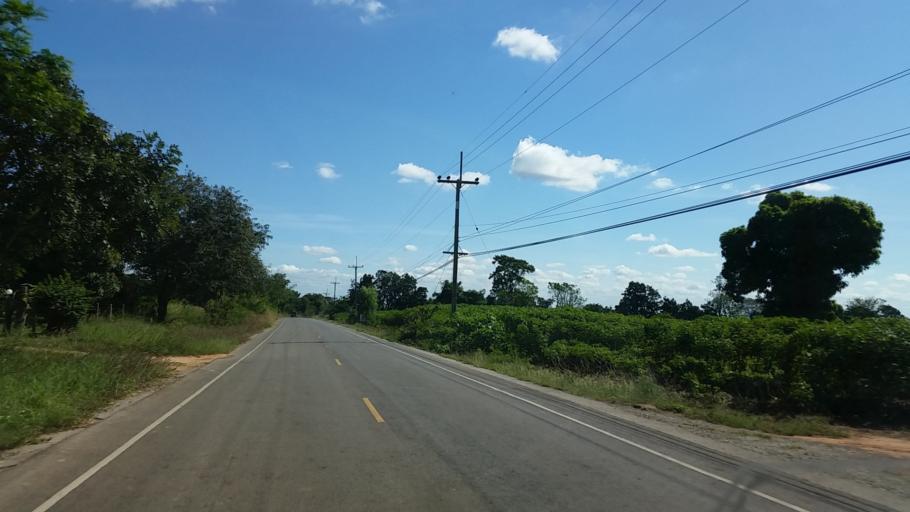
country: TH
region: Chaiyaphum
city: Thep Sathit
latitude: 15.5719
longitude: 101.4138
